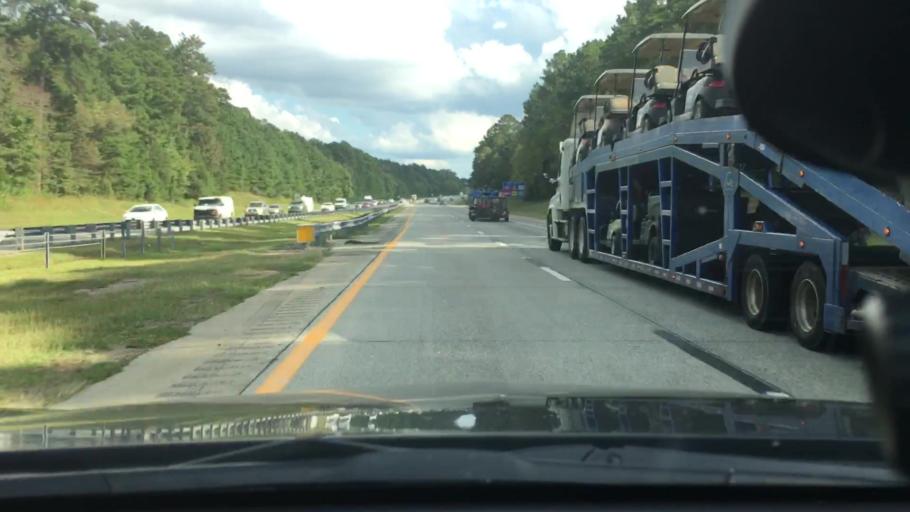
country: US
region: North Carolina
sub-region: Orange County
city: Chapel Hill
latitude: 35.9586
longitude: -79.0101
